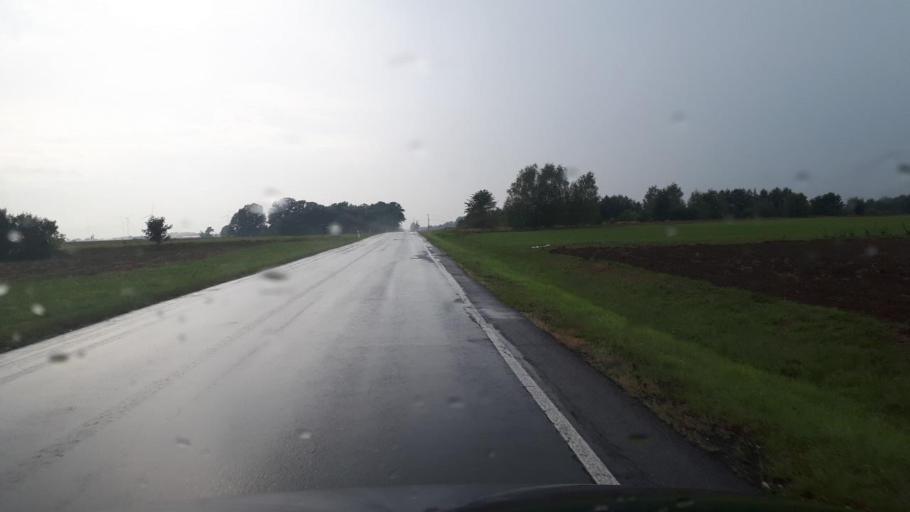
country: PL
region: Silesian Voivodeship
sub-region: Powiat gliwicki
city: Wielowies
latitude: 50.5283
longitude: 18.6453
